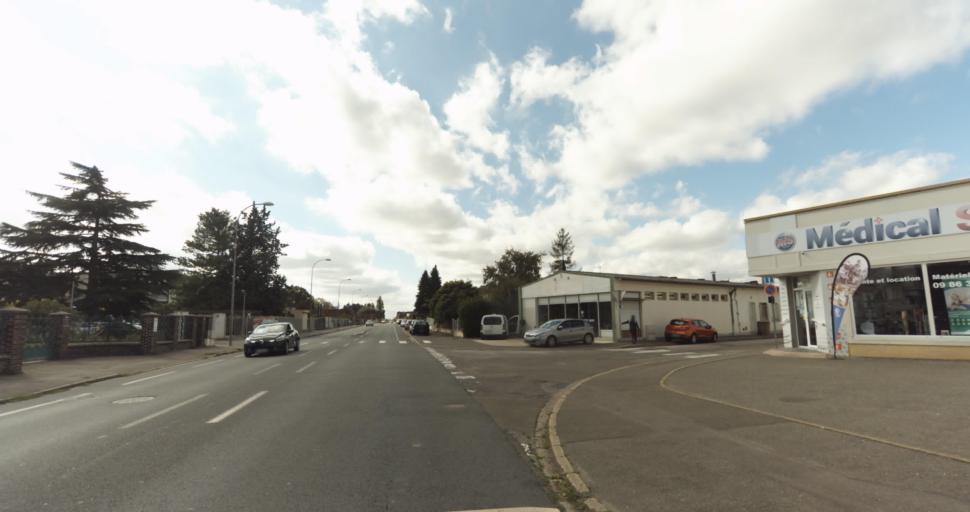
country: FR
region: Centre
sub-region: Departement d'Eure-et-Loir
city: Garnay
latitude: 48.7274
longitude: 1.3328
